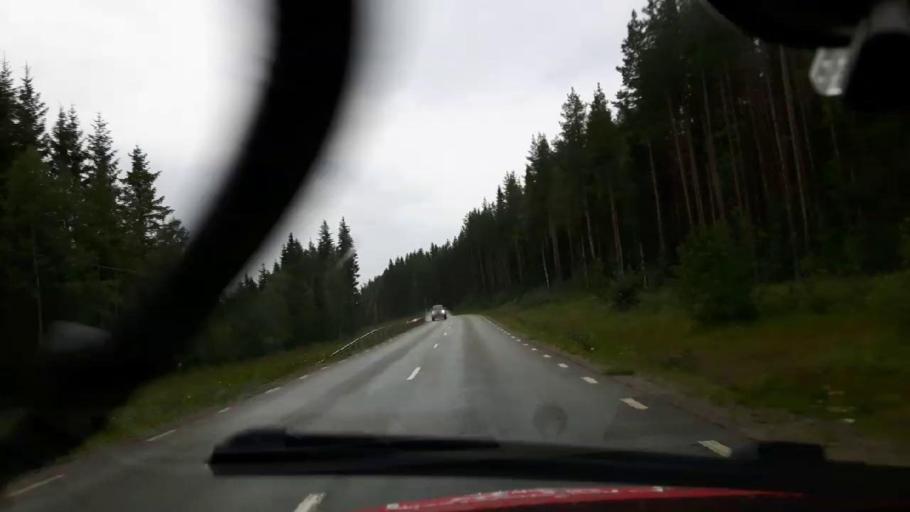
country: SE
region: Jaemtland
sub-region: OEstersunds Kommun
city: Brunflo
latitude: 62.8356
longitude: 15.0070
